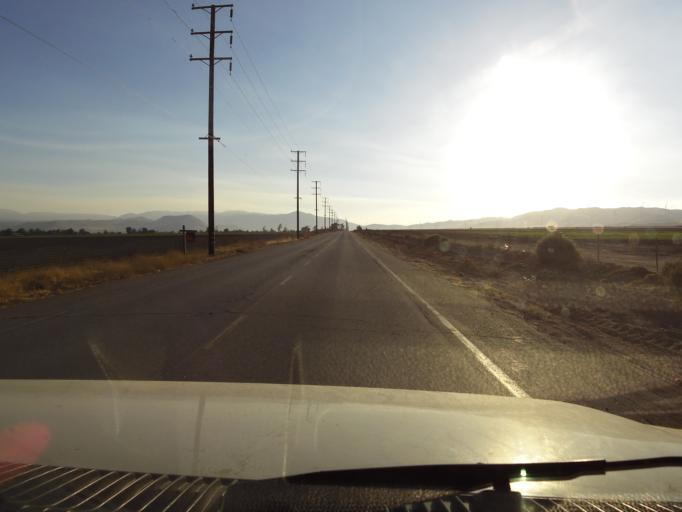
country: US
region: California
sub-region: Kern County
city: Tehachapi
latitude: 35.1097
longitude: -118.4206
